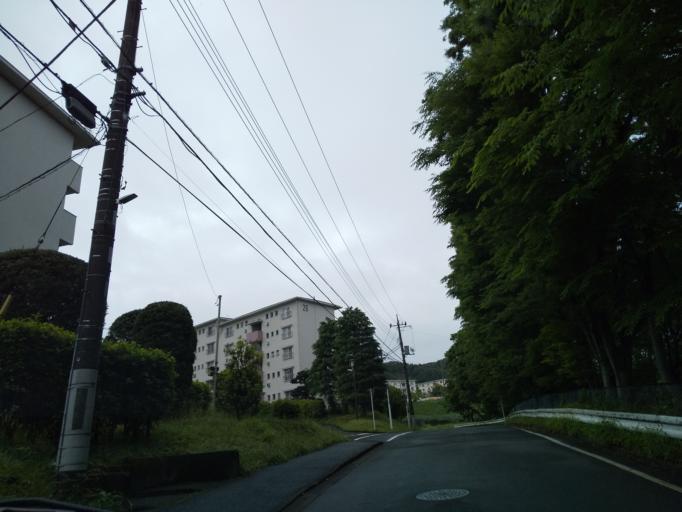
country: JP
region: Tokyo
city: Hino
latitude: 35.6556
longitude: 139.4142
